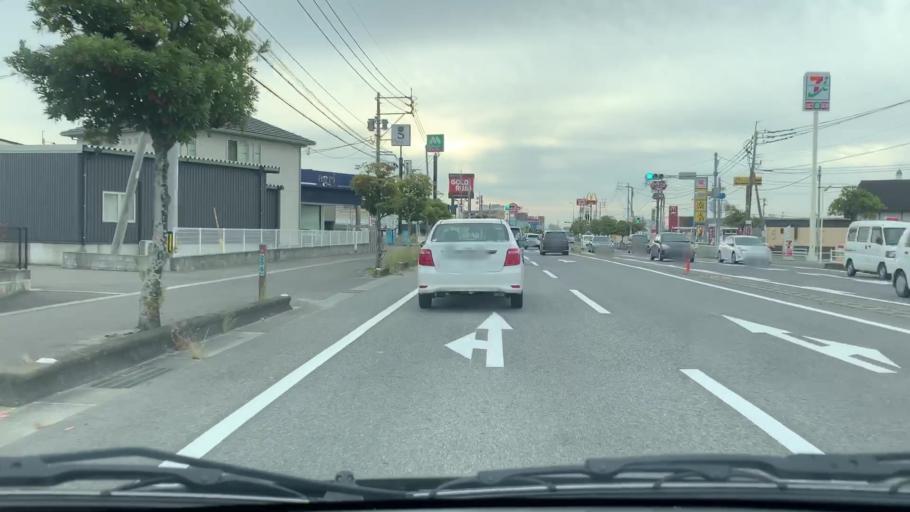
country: JP
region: Saga Prefecture
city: Saga-shi
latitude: 33.2950
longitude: 130.2835
